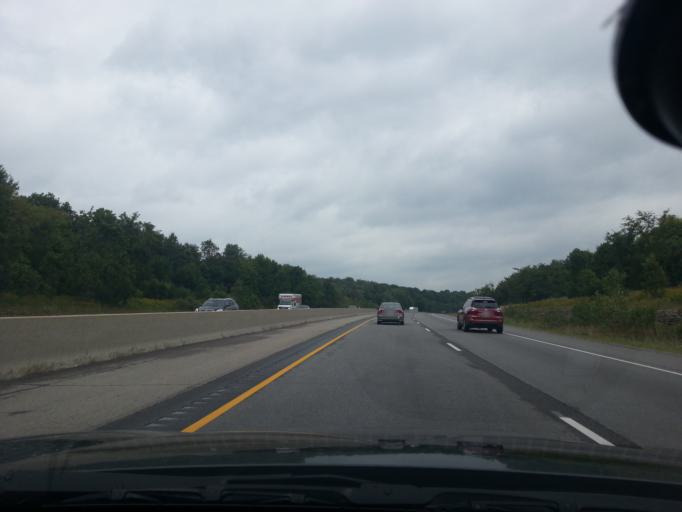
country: CA
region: Ontario
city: Brockville
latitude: 44.5450
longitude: -75.7677
